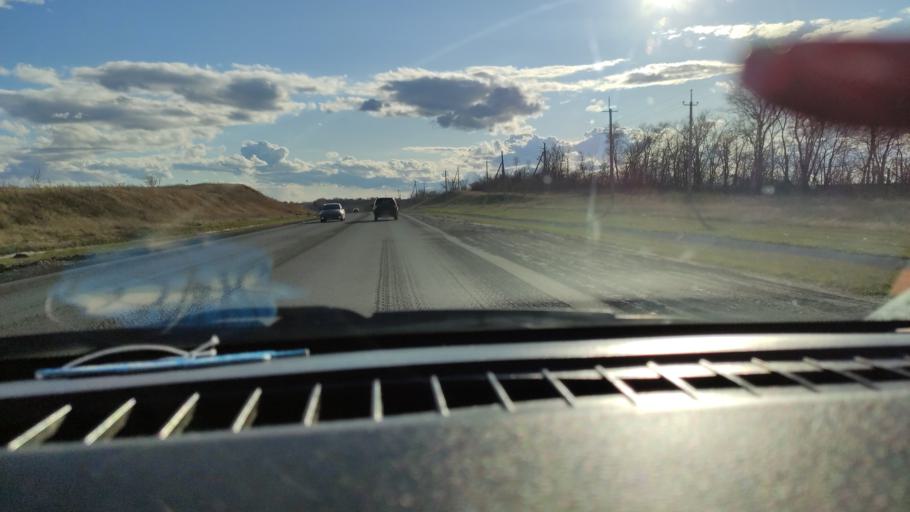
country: RU
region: Saratov
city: Shumeyka
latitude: 51.7789
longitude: 46.1209
